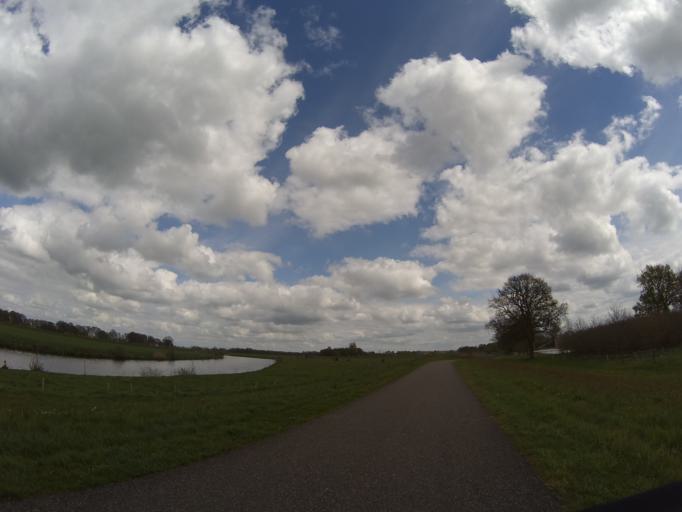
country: NL
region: Overijssel
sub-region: Gemeente Dalfsen
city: Dalfsen
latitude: 52.5184
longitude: 6.1930
